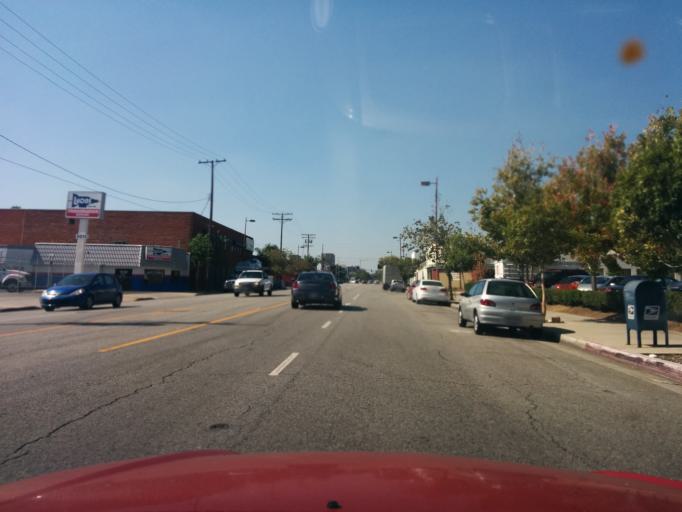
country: US
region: California
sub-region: Los Angeles County
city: Burbank
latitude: 34.1727
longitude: -118.2974
